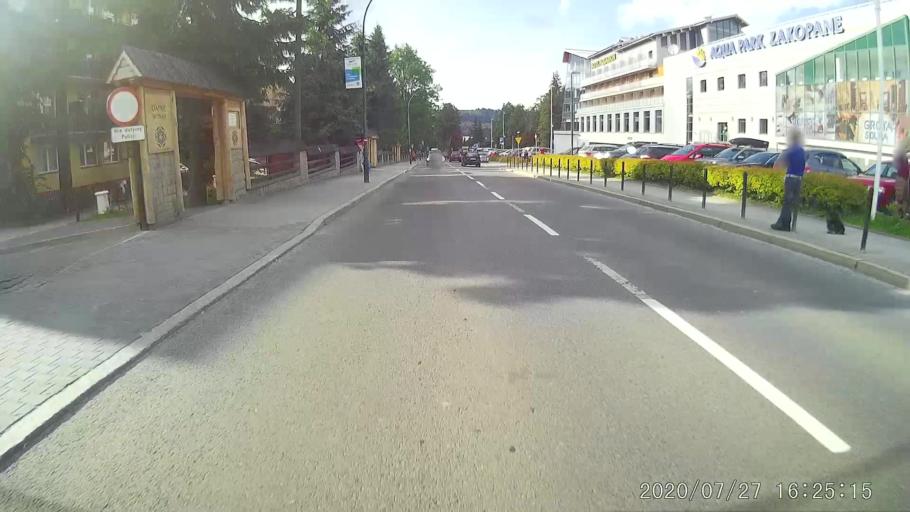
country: PL
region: Lesser Poland Voivodeship
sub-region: Powiat tatrzanski
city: Zakopane
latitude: 49.2950
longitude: 19.9643
